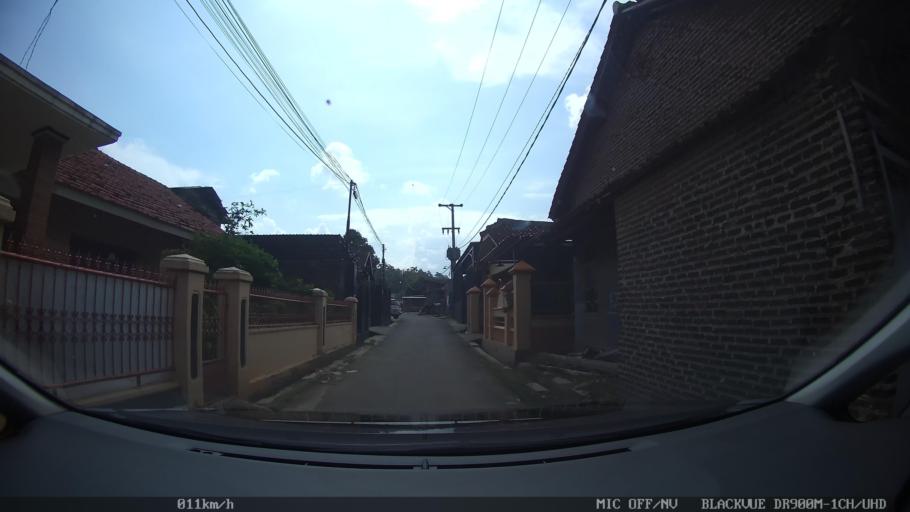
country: ID
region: Lampung
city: Kedaton
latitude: -5.3970
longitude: 105.2311
